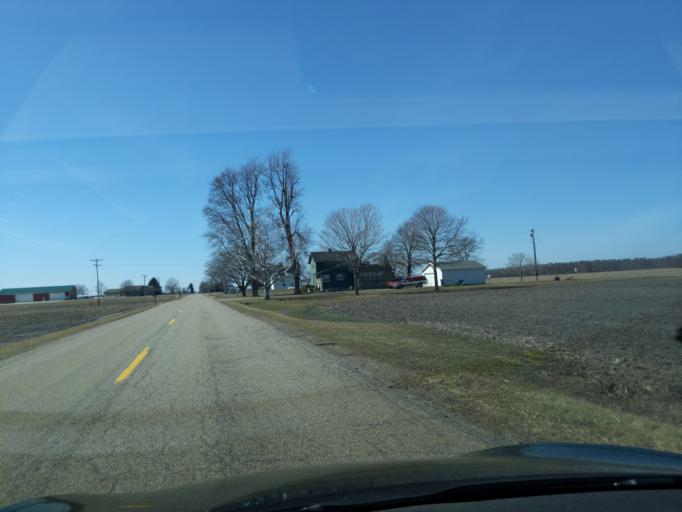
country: US
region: Michigan
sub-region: Ionia County
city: Portland
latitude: 42.7266
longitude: -84.9280
